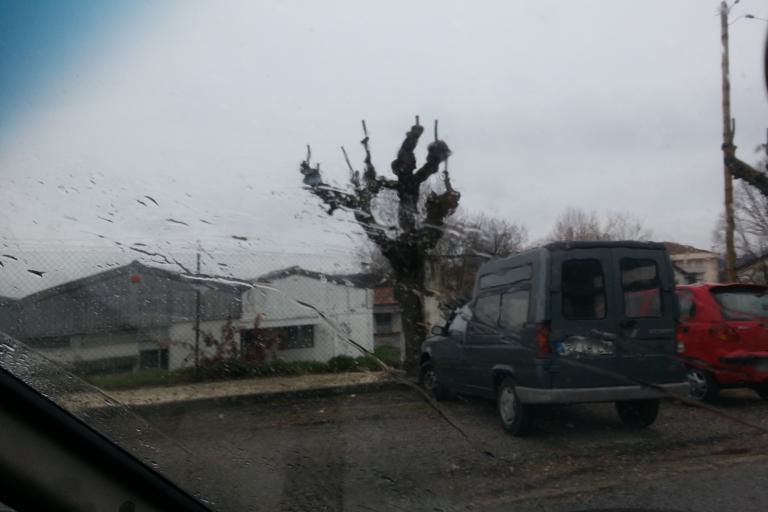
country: PT
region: Viseu
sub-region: Viseu
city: Rio de Loba
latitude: 40.6703
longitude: -7.8860
